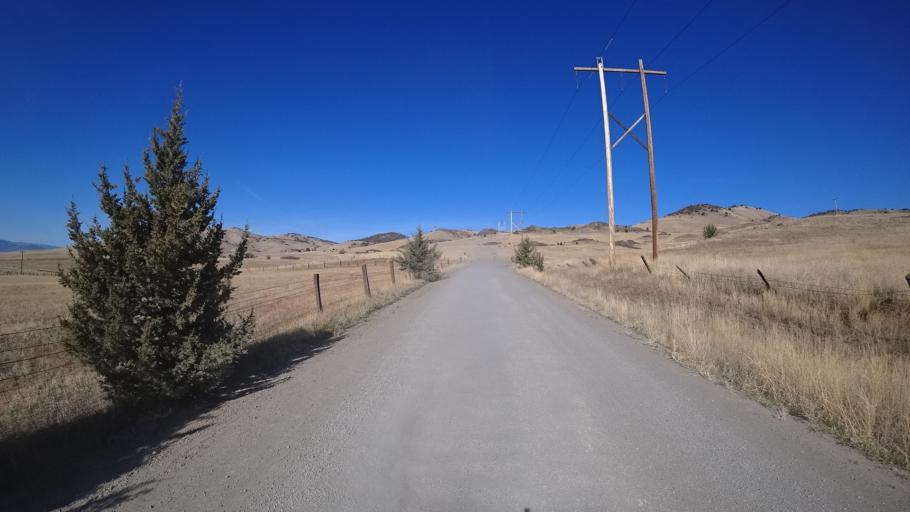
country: US
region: California
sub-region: Siskiyou County
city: Montague
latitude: 41.8290
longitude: -122.3623
